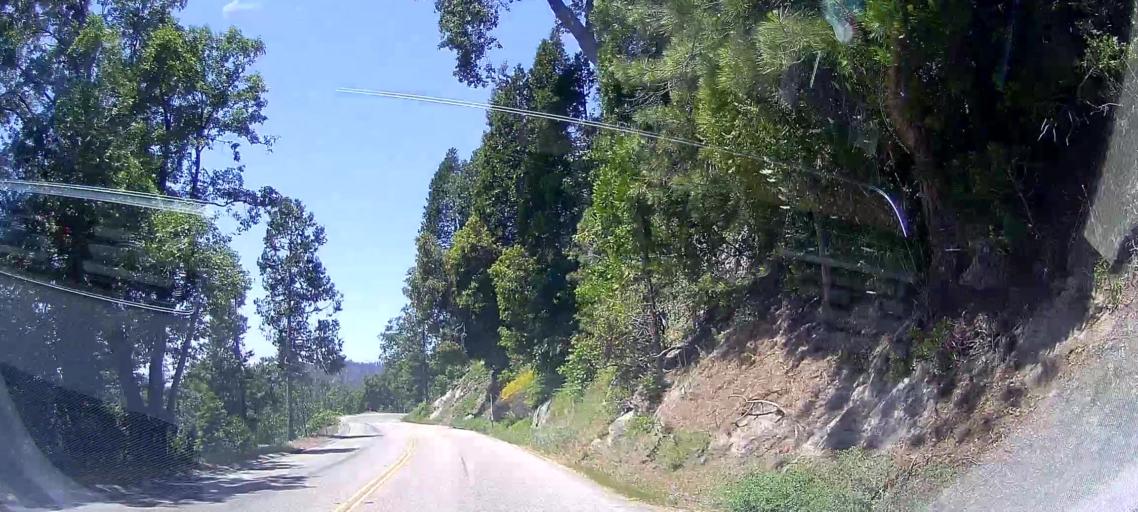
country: US
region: California
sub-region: Fresno County
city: Squaw Valley
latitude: 36.7171
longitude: -118.9826
